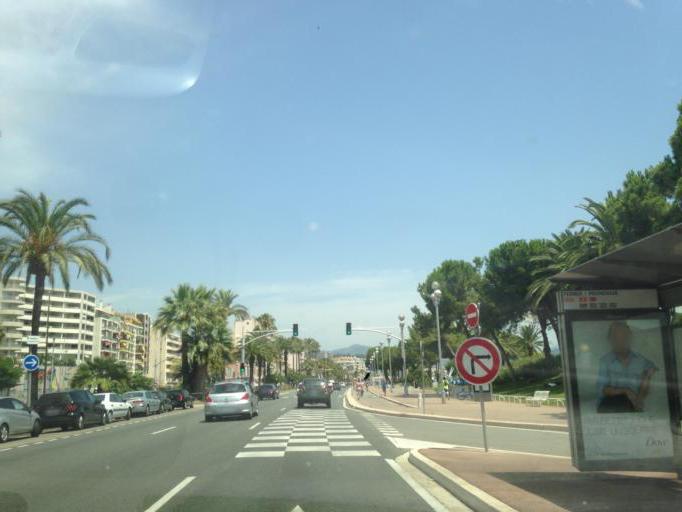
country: FR
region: Provence-Alpes-Cote d'Azur
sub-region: Departement des Alpes-Maritimes
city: Nice
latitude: 43.6770
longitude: 7.2288
